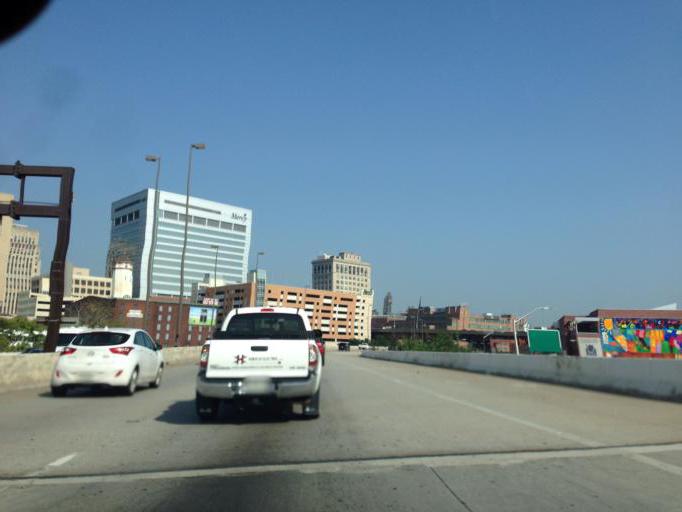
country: US
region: Maryland
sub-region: City of Baltimore
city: Baltimore
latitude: 39.2925
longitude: -76.6084
